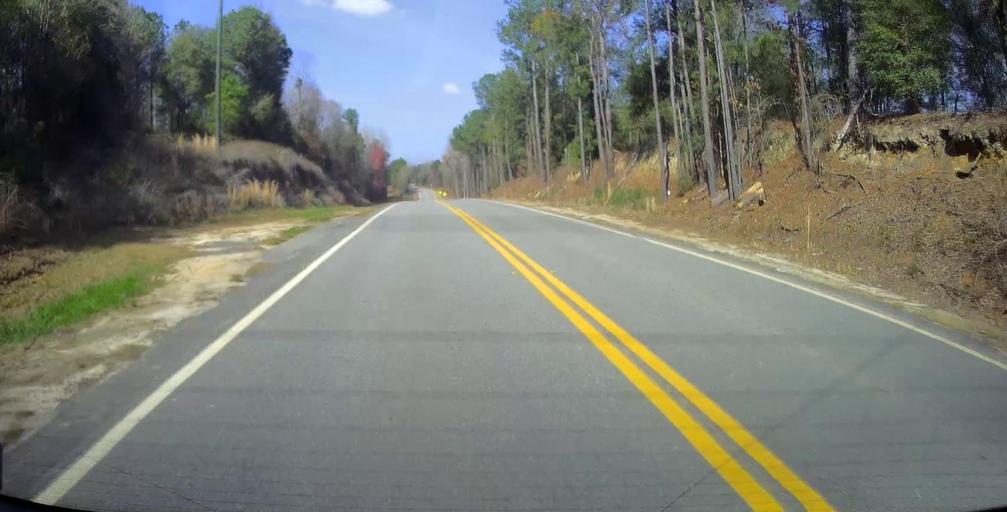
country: US
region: Georgia
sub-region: Twiggs County
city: Jeffersonville
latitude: 32.7806
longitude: -83.3313
